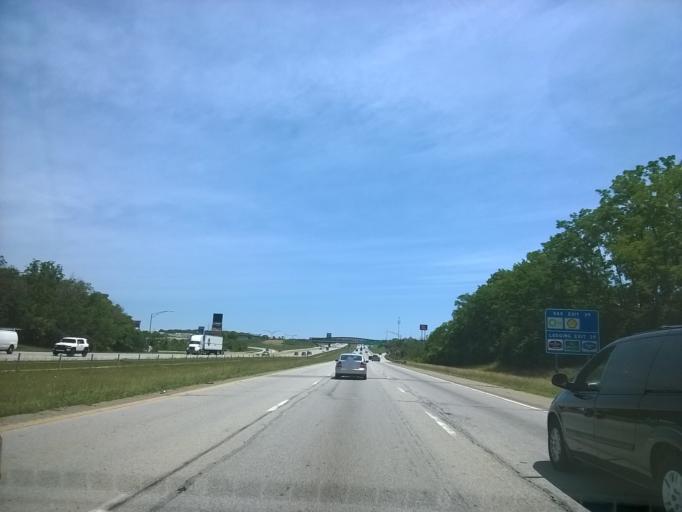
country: US
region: Ohio
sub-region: Hamilton County
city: Pleasant Run Farm
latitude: 39.2972
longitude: -84.5321
